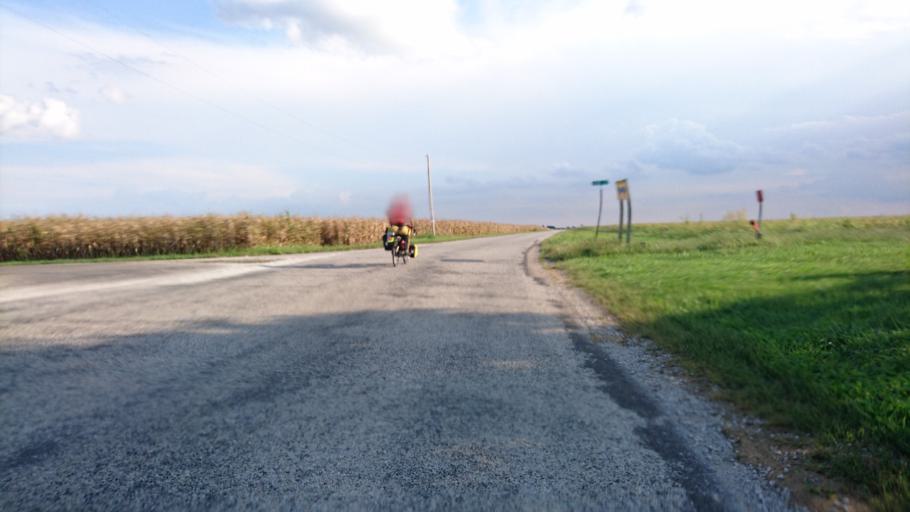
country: US
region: Illinois
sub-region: Logan County
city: Atlanta
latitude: 40.2587
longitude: -89.2053
